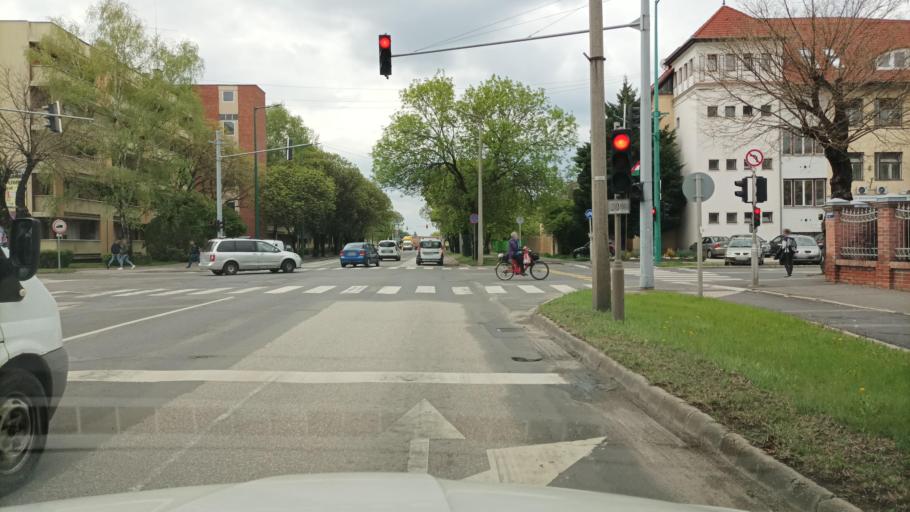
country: HU
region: Pest
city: Cegled
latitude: 47.1764
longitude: 19.8007
